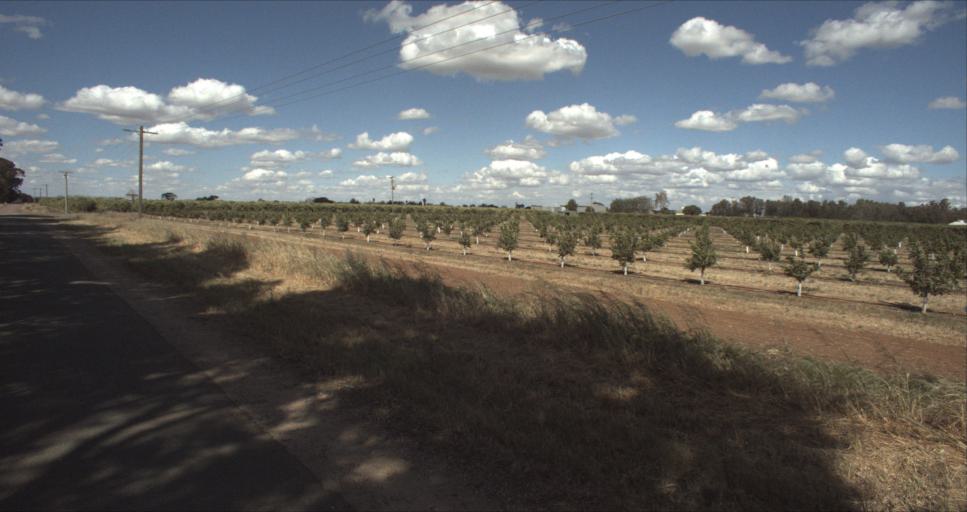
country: AU
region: New South Wales
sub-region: Leeton
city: Leeton
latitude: -34.5096
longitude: 146.2303
